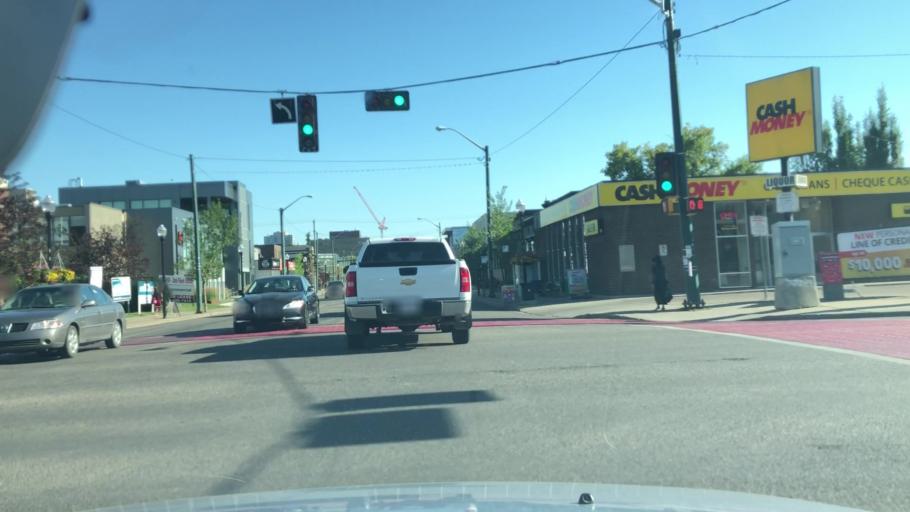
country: CA
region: Alberta
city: Edmonton
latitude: 53.5511
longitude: -113.5359
